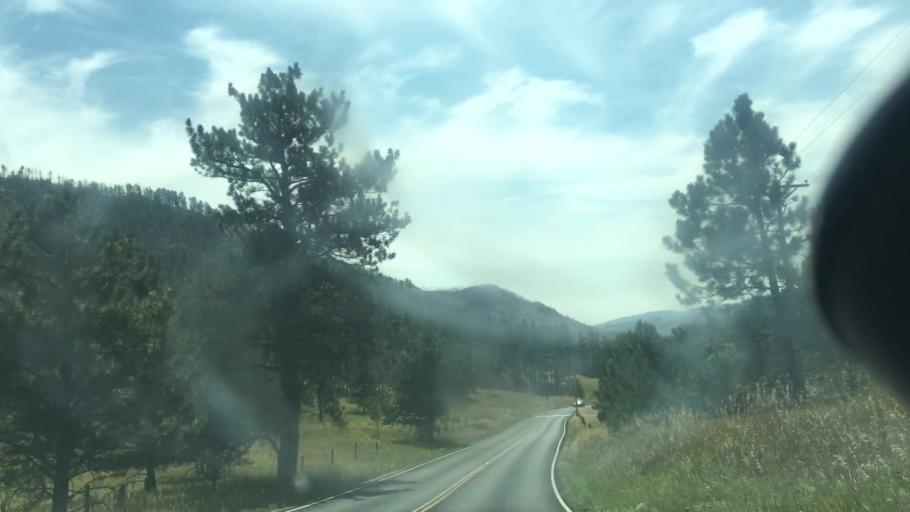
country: US
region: Colorado
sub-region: Larimer County
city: Laporte
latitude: 40.6022
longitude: -105.3419
